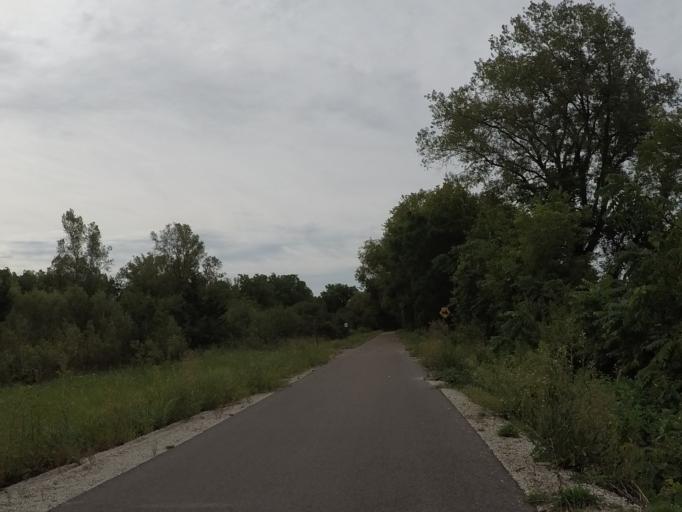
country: US
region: Wisconsin
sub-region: Sauk County
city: Prairie du Sac
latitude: 43.3482
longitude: -89.7407
